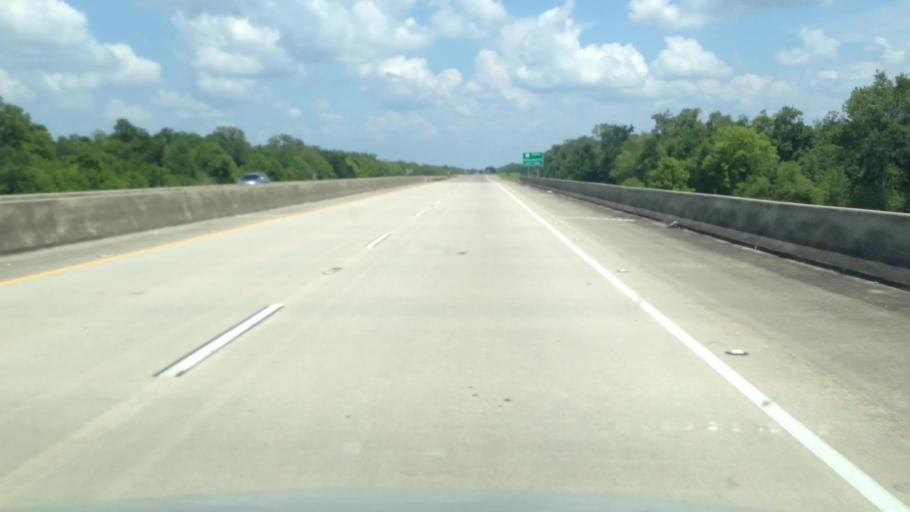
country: US
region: Louisiana
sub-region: Saint Landry Parish
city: Krotz Springs
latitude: 30.5476
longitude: -91.8263
